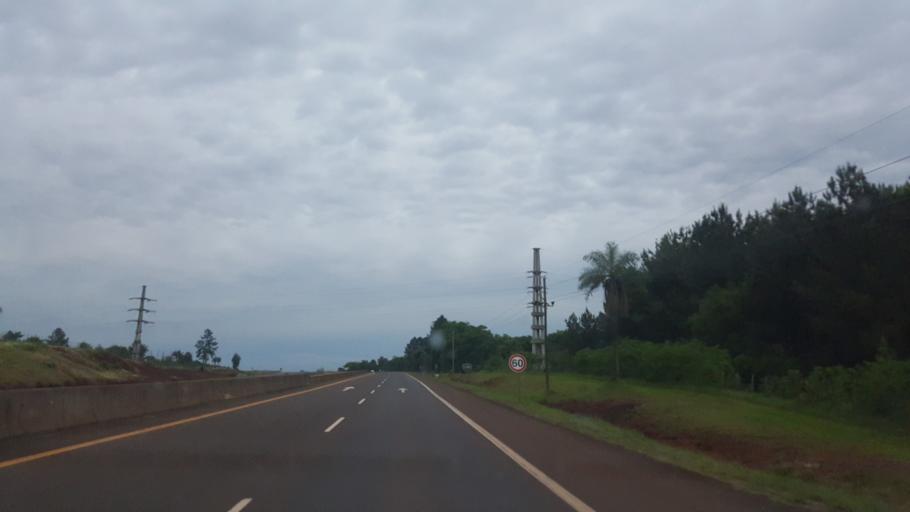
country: AR
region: Misiones
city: Garupa
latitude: -27.5407
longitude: -55.8533
